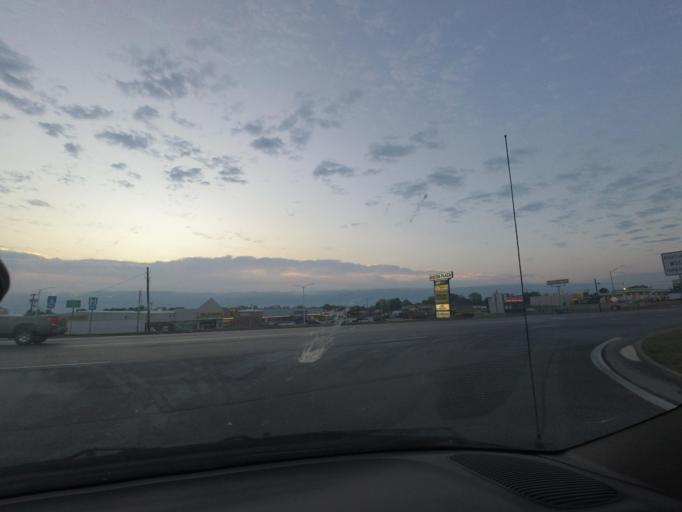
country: US
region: Missouri
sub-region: Macon County
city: Macon
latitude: 39.7528
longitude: -92.4692
